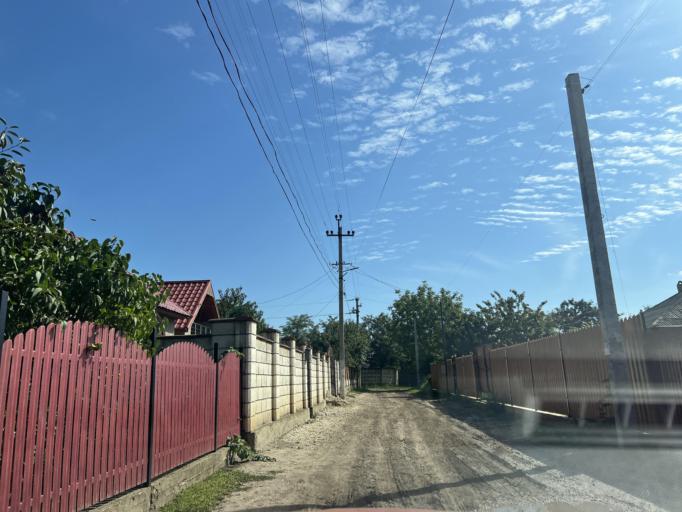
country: MD
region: Ungheni
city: Ungheni
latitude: 47.1986
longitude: 27.8151
